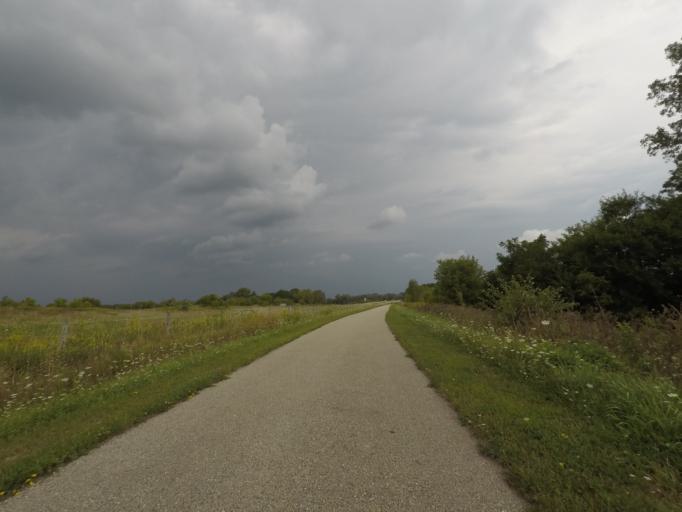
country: US
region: Wisconsin
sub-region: Jefferson County
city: Fort Atkinson
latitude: 42.9592
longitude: -88.8278
